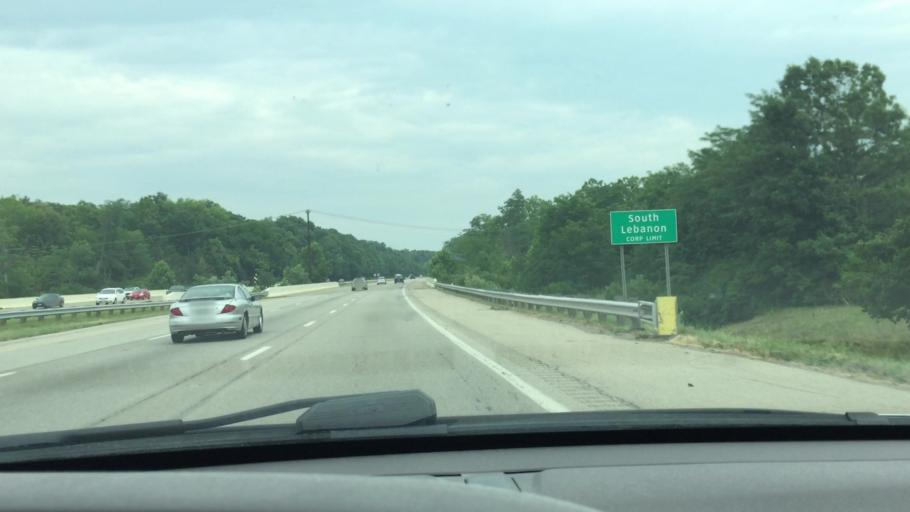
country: US
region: Ohio
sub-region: Warren County
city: South Lebanon
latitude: 39.3795
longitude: -84.2364
